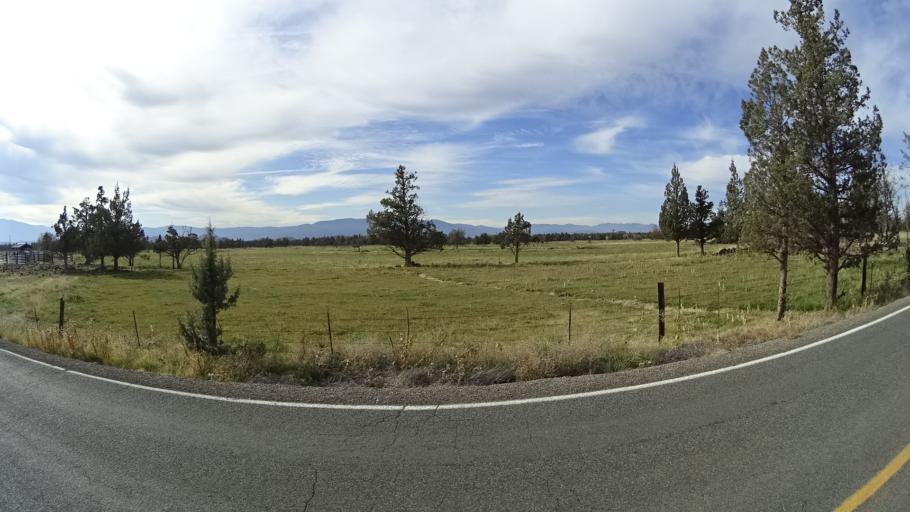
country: US
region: California
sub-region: Siskiyou County
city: Montague
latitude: 41.6362
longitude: -122.3995
